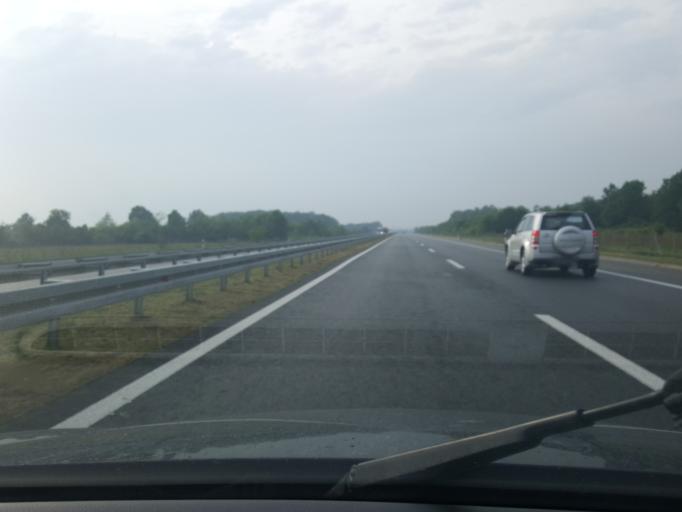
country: RS
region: Central Serbia
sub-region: Kolubarski Okrug
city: Lajkovac
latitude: 44.3836
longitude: 20.1118
